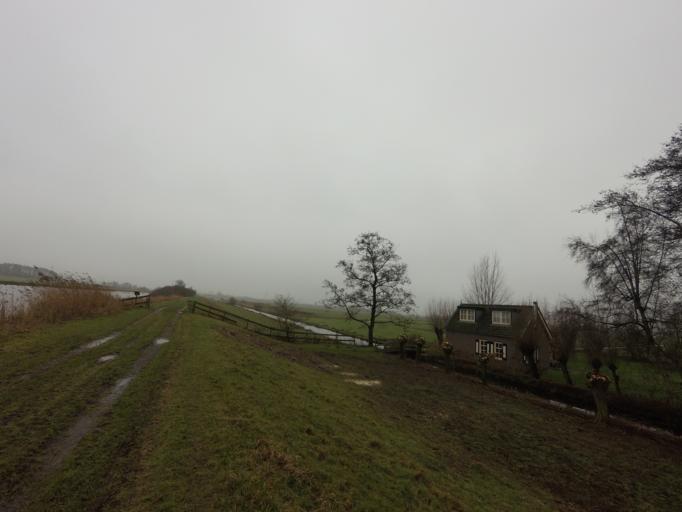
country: NL
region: South Holland
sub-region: Gemeente Vlist
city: Haastrecht
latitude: 52.0289
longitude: 4.7904
